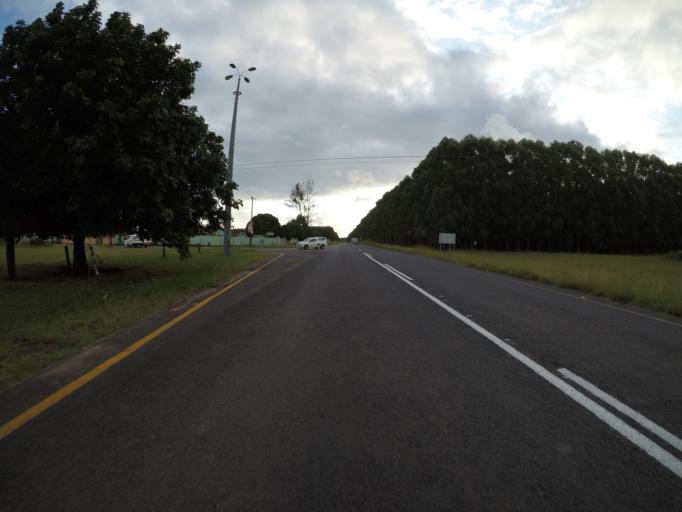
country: ZA
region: KwaZulu-Natal
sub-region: uMkhanyakude District Municipality
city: Mtubatuba
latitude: -28.3976
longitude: 32.2149
